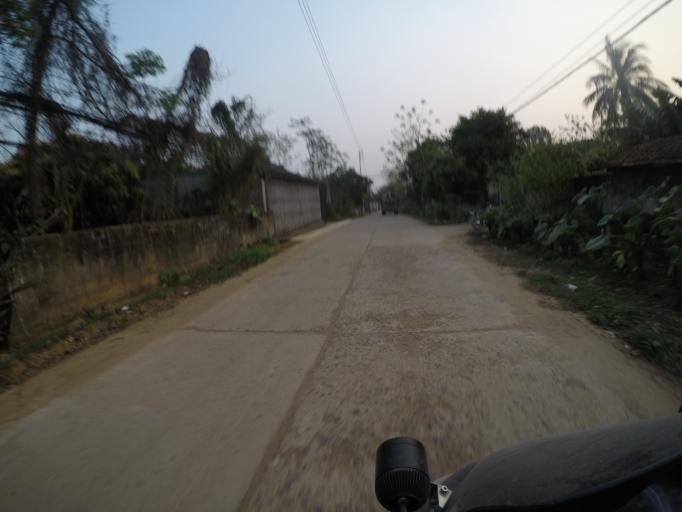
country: VN
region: Vinh Phuc
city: Trai Ngau
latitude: 21.4643
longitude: 105.5705
